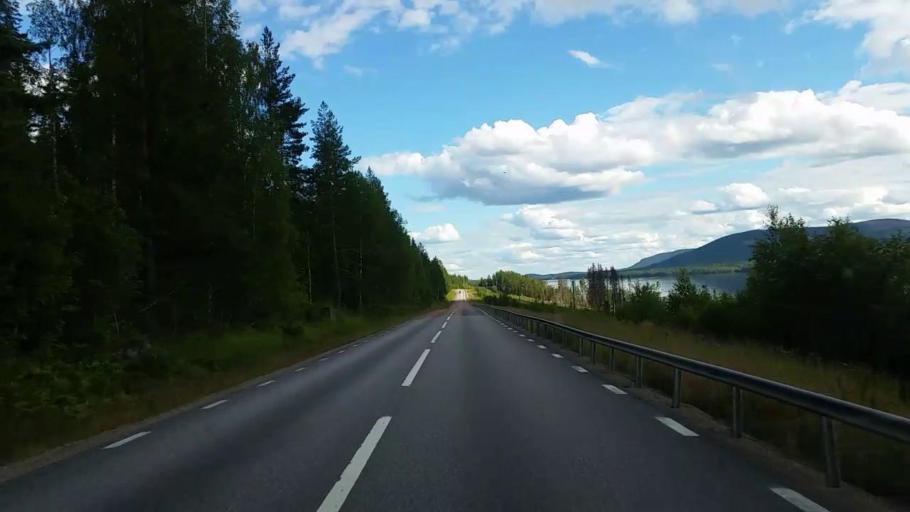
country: SE
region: Gaevleborg
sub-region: Ljusdals Kommun
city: Farila
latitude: 62.1089
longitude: 15.7697
